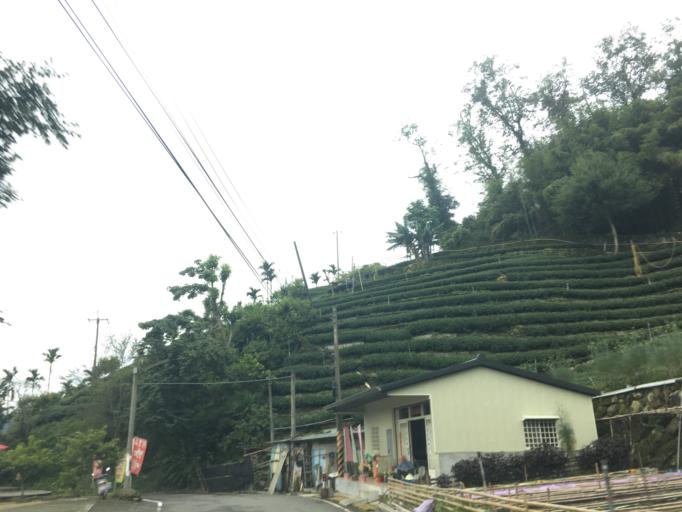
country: TW
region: Taiwan
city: Lugu
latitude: 23.5411
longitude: 120.7151
